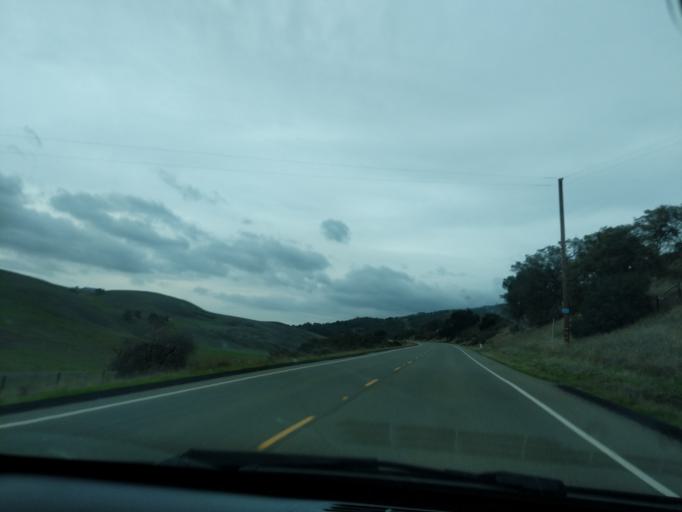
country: US
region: California
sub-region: Monterey County
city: Soledad
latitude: 36.6216
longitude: -121.2206
